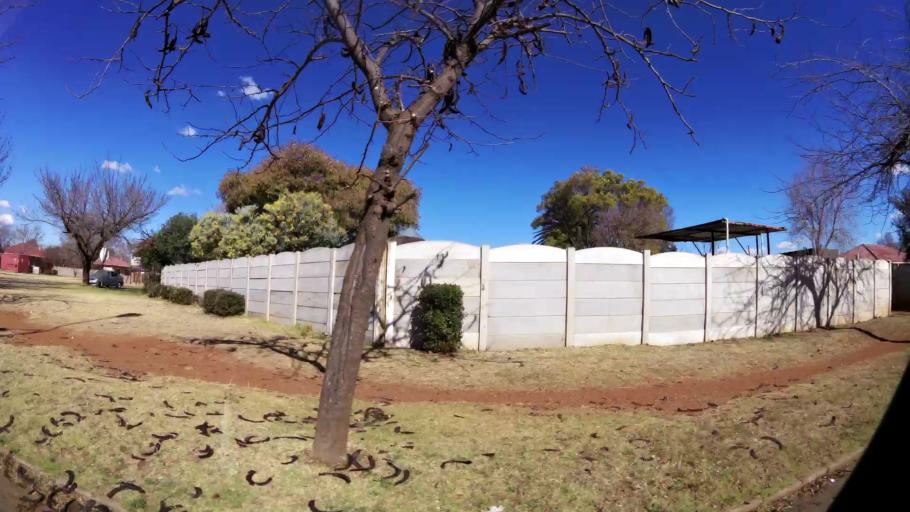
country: ZA
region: Gauteng
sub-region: West Rand District Municipality
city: Carletonville
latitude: -26.3626
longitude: 27.3926
